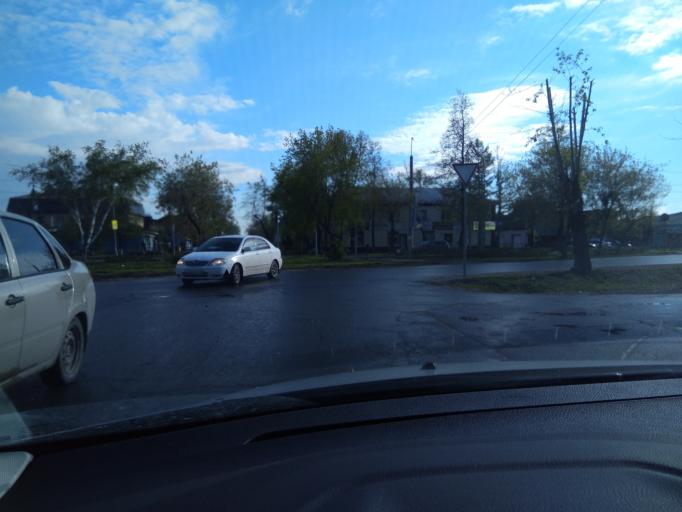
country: RU
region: Tjumen
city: Tyumen
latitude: 57.1387
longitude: 65.5195
